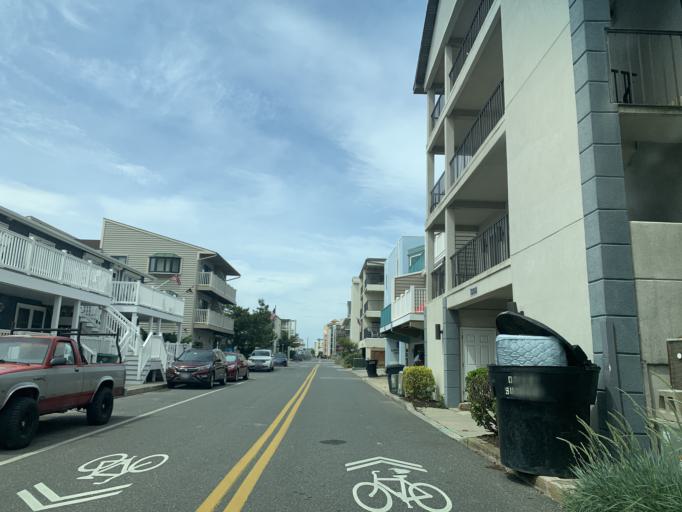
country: US
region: Delaware
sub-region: Sussex County
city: Bethany Beach
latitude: 38.4415
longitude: -75.0514
